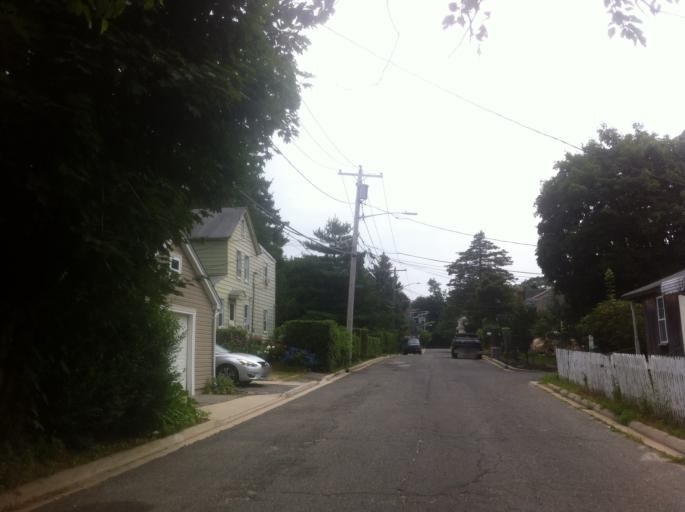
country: US
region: New York
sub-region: Nassau County
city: Locust Valley
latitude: 40.8774
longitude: -73.6116
